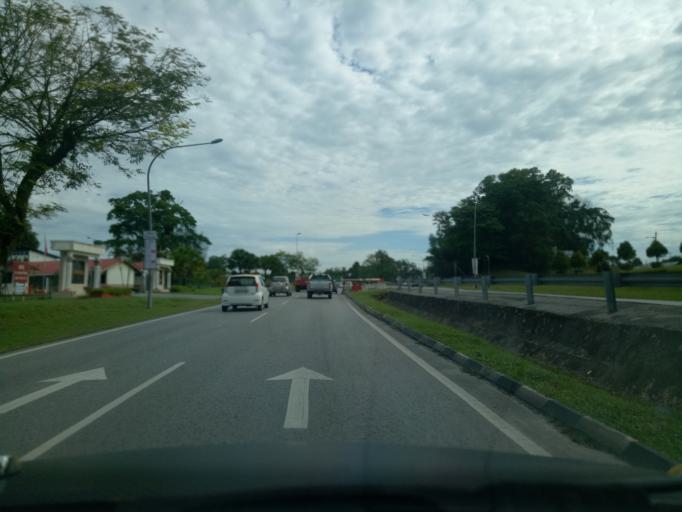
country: MY
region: Sarawak
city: Kuching
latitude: 1.4557
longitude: 110.3250
